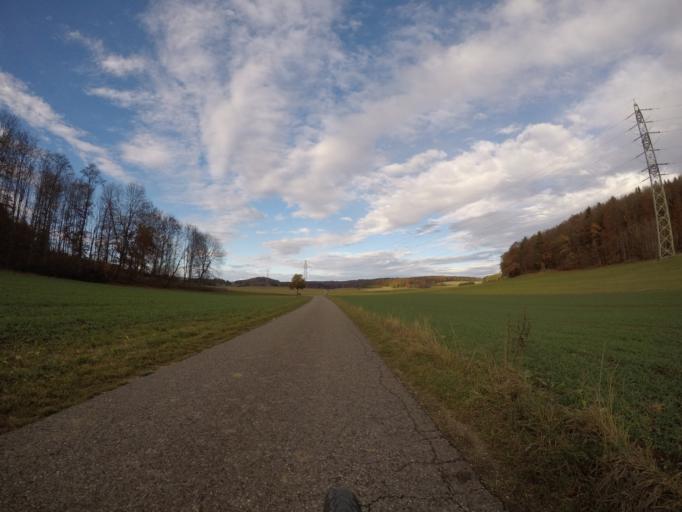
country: DE
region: Baden-Wuerttemberg
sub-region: Tuebingen Region
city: Sankt Johann
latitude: 48.4602
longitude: 9.3157
